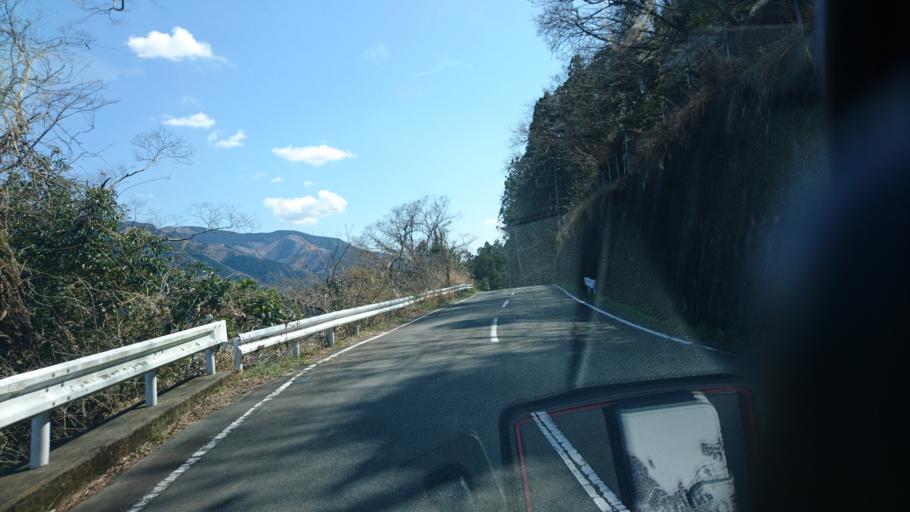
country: JP
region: Shizuoka
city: Fujinomiya
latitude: 35.3504
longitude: 138.4373
